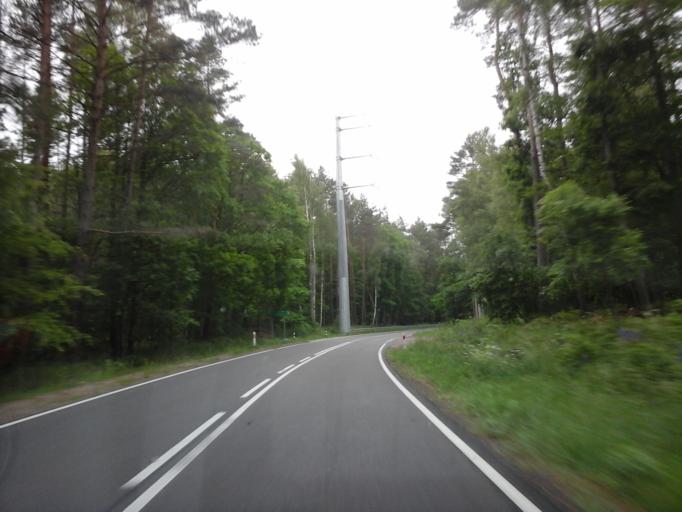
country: PL
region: West Pomeranian Voivodeship
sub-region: Powiat drawski
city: Czaplinek
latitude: 53.5011
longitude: 16.2220
